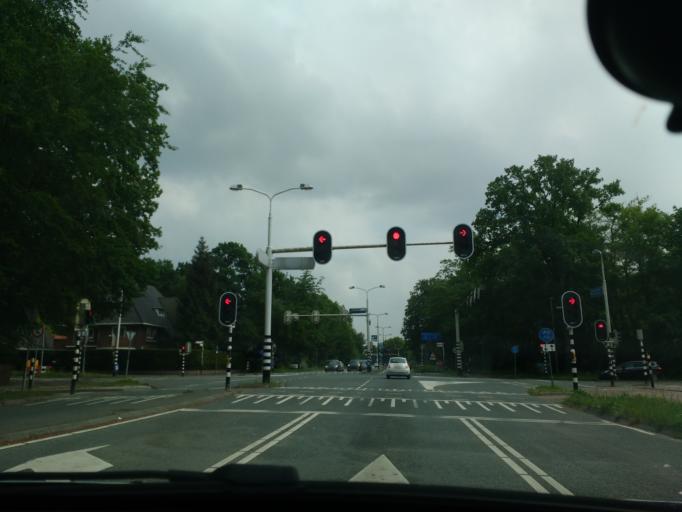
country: NL
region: North Holland
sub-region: Gemeente Bussum
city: Bussum
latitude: 52.2832
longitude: 5.1791
